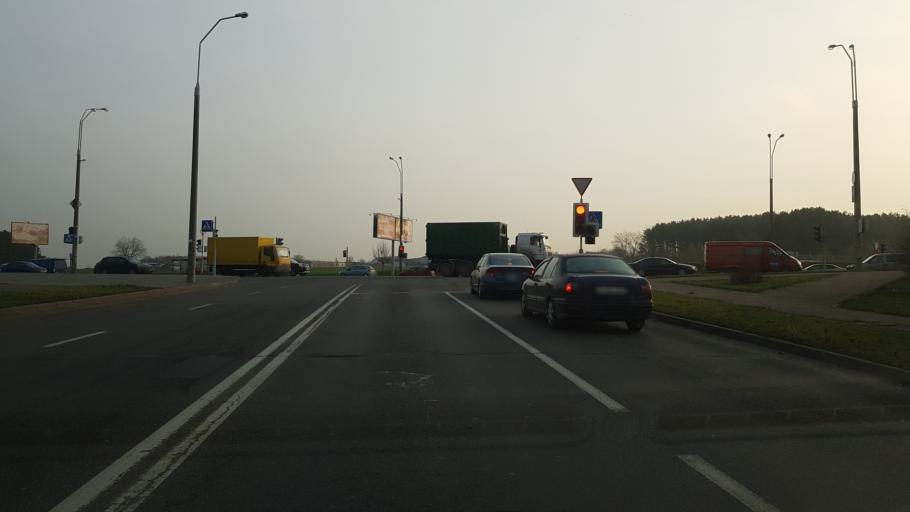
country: BY
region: Minsk
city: Bal'shavik
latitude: 53.9630
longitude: 27.5358
